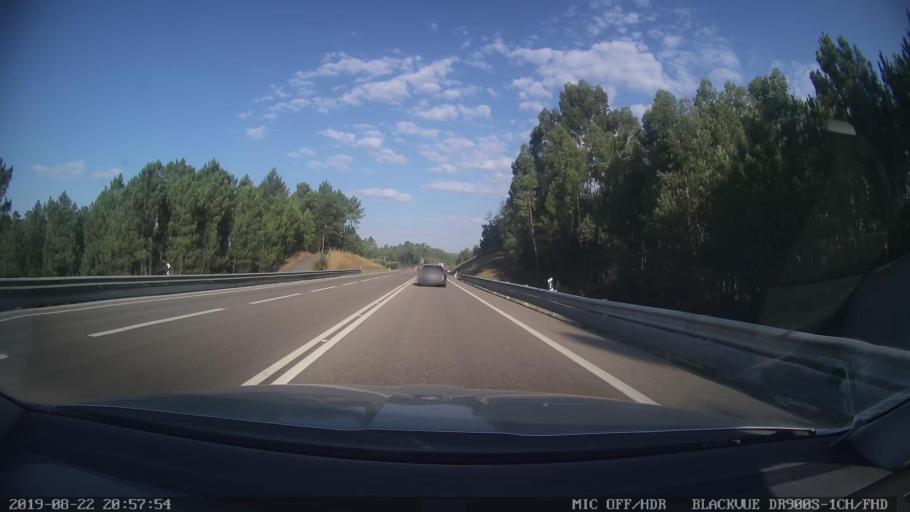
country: PT
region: Castelo Branco
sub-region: Serta
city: Serta
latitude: 39.7968
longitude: -8.0736
